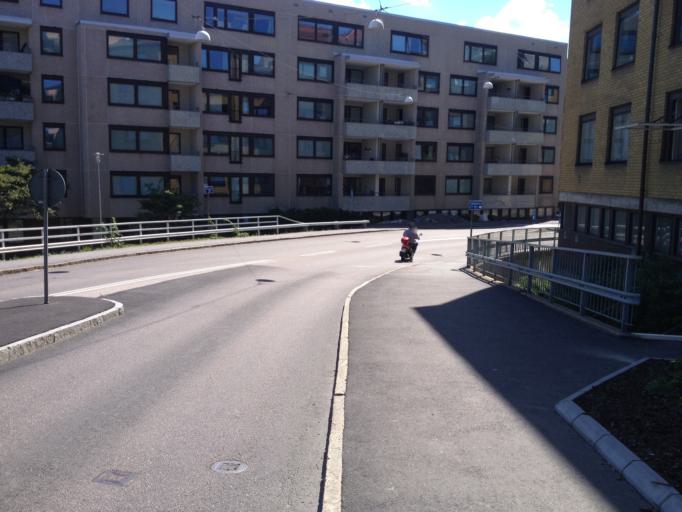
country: SE
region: Vaestra Goetaland
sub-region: Goteborg
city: Goeteborg
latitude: 57.6961
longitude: 11.9456
